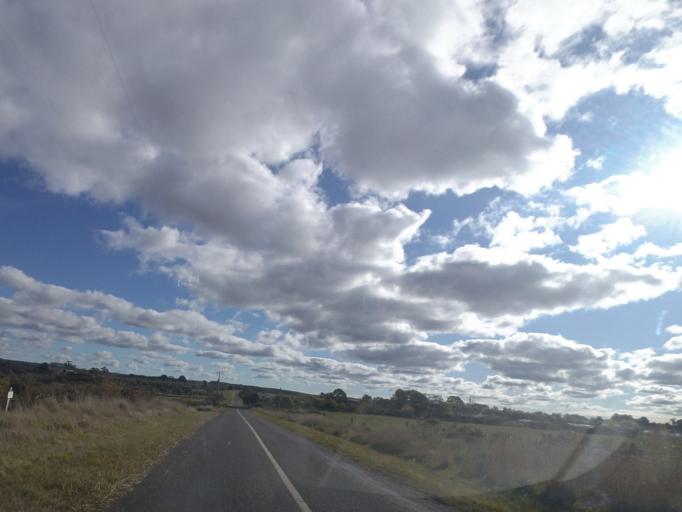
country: AU
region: Victoria
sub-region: Mount Alexander
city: Castlemaine
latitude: -37.2507
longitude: 144.3962
